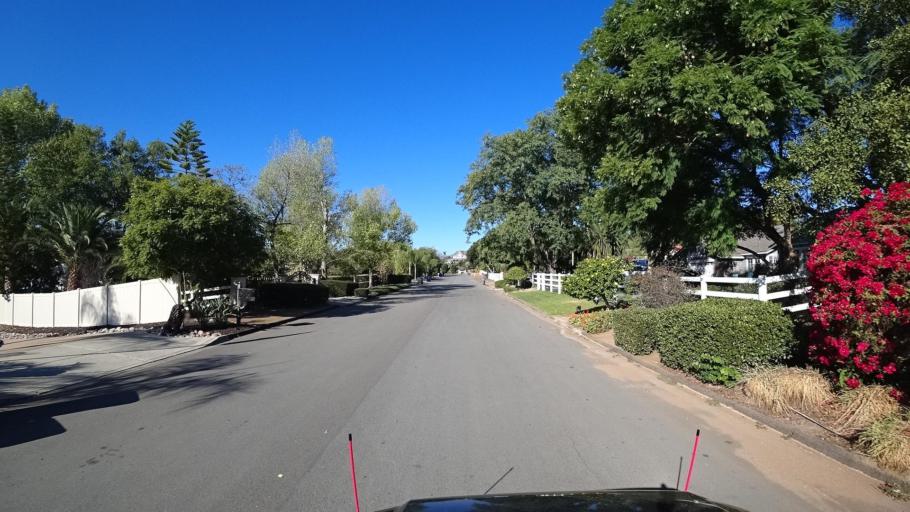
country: US
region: California
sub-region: San Diego County
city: Jamul
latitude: 32.7096
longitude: -116.8745
